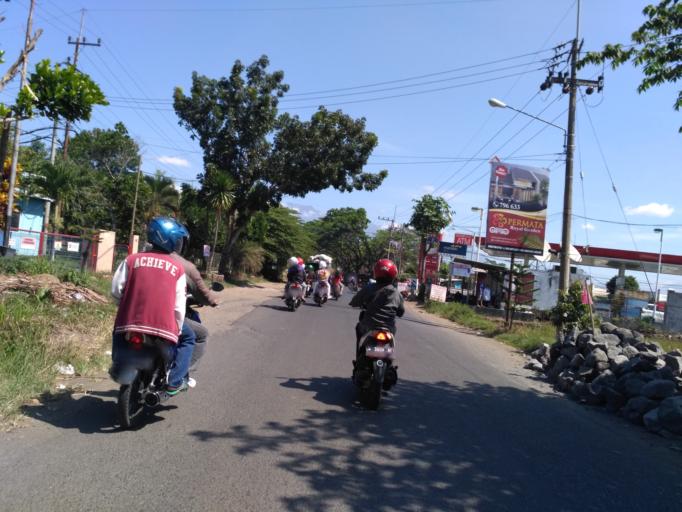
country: ID
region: East Java
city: Malang
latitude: -7.9672
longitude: 112.6810
